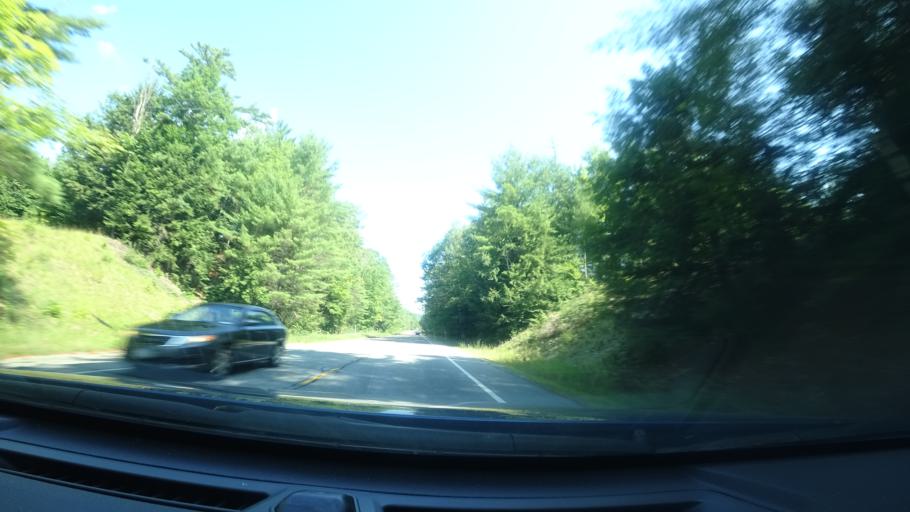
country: US
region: New York
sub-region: Warren County
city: Warrensburg
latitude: 43.5982
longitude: -73.8014
